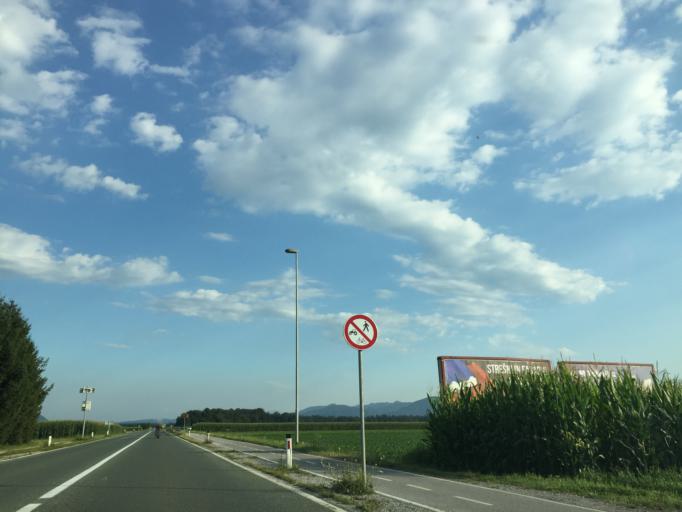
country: SI
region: Kranj
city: Kranj
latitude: 46.2196
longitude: 14.3602
